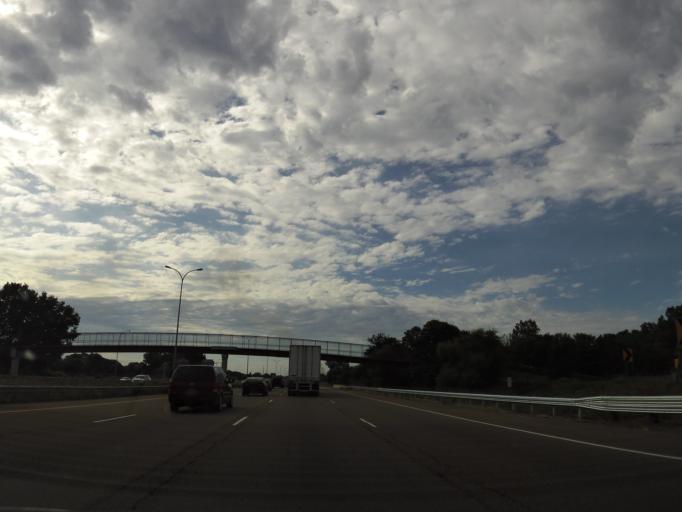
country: US
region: Minnesota
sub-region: Hennepin County
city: Brooklyn Center
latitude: 45.0713
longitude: -93.3080
